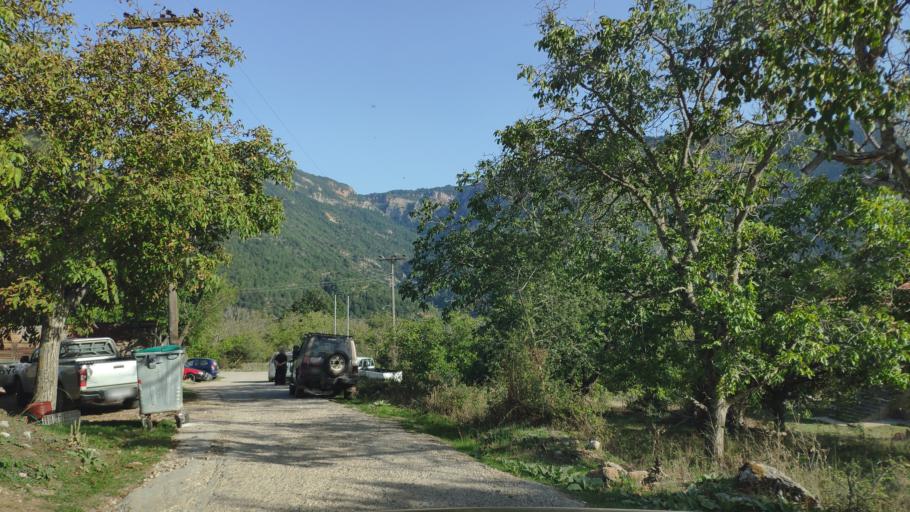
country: GR
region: West Greece
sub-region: Nomos Achaias
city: Aiyira
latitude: 37.9914
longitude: 22.3531
